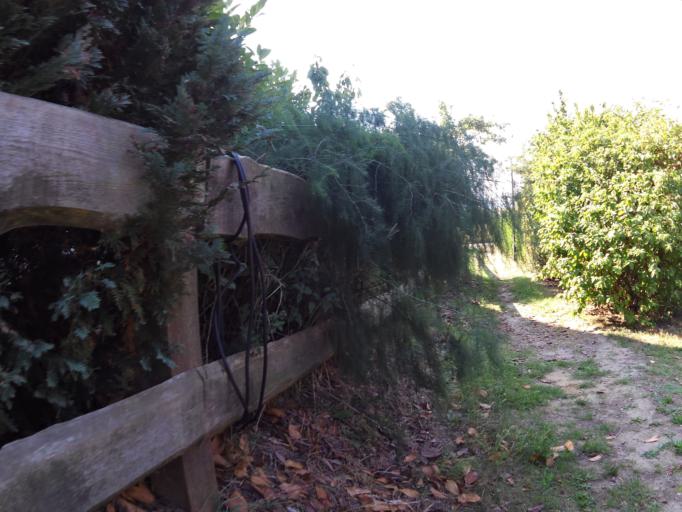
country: DE
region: Mecklenburg-Vorpommern
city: Loddin
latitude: 54.0133
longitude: 14.0433
